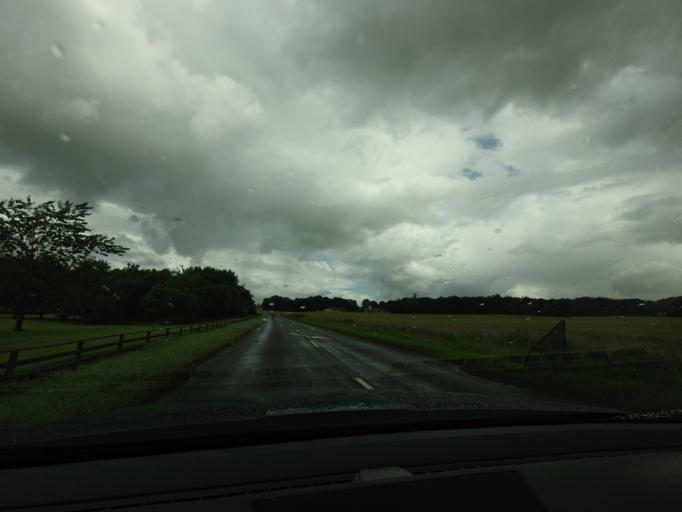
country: GB
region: Scotland
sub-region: Aberdeenshire
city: Turriff
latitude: 57.5544
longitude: -2.4396
